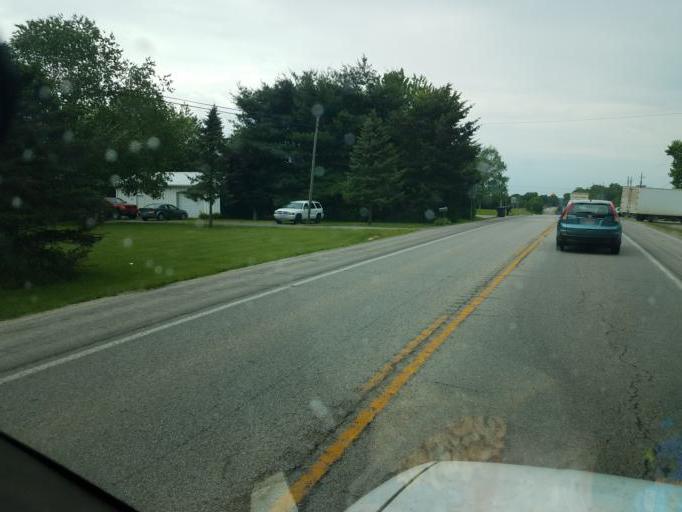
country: US
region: Ohio
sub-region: Wayne County
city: Apple Creek
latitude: 40.7371
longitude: -81.8166
